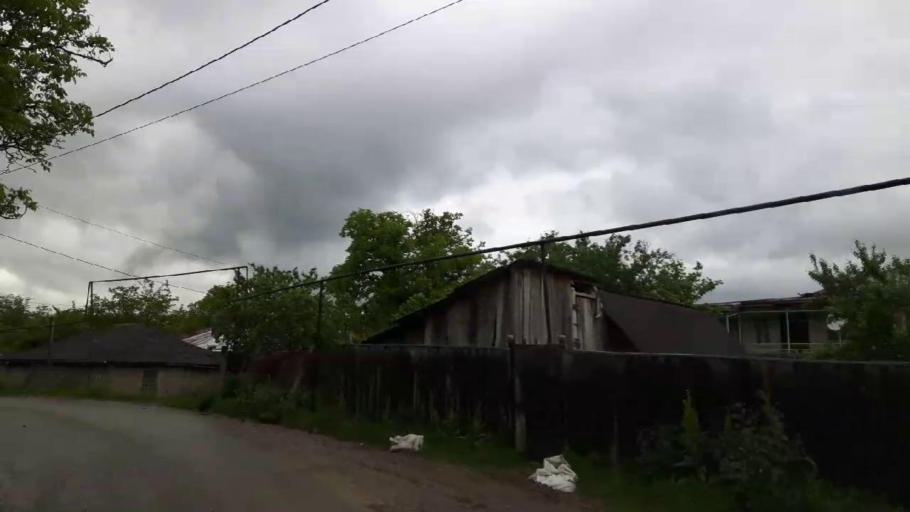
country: GE
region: Shida Kartli
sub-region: Khashuris Raioni
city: Khashuri
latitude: 41.9826
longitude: 43.6690
